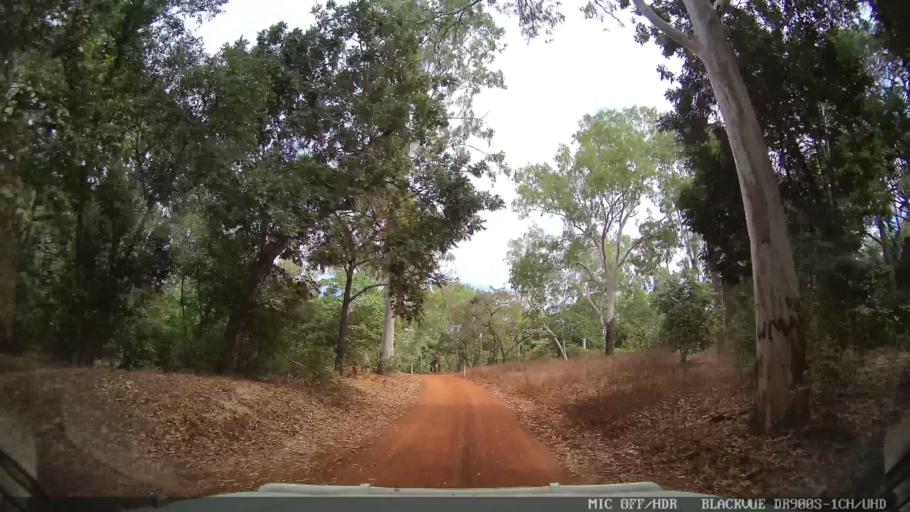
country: AU
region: Queensland
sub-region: Cook
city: Cooktown
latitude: -15.2910
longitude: 144.8443
